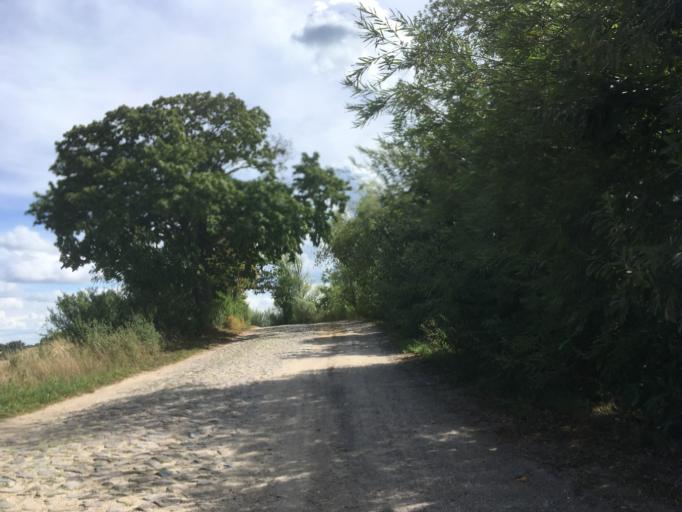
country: DE
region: Brandenburg
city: Gerswalde
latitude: 53.1282
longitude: 13.8018
